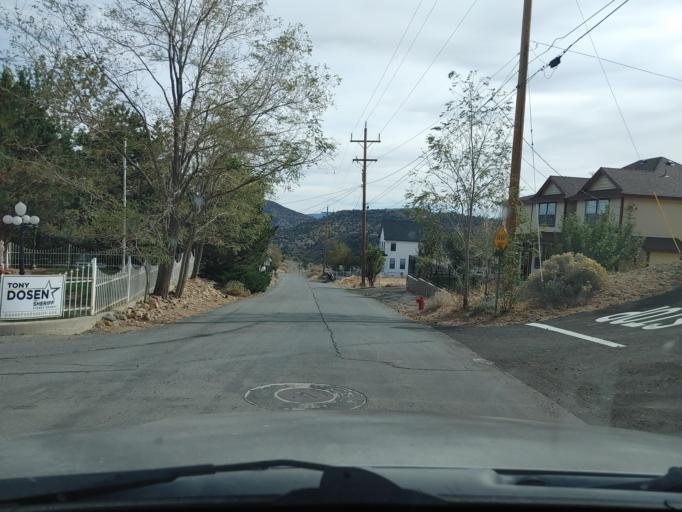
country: US
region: Nevada
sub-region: Storey County
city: Virginia City
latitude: 39.3118
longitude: -119.6427
